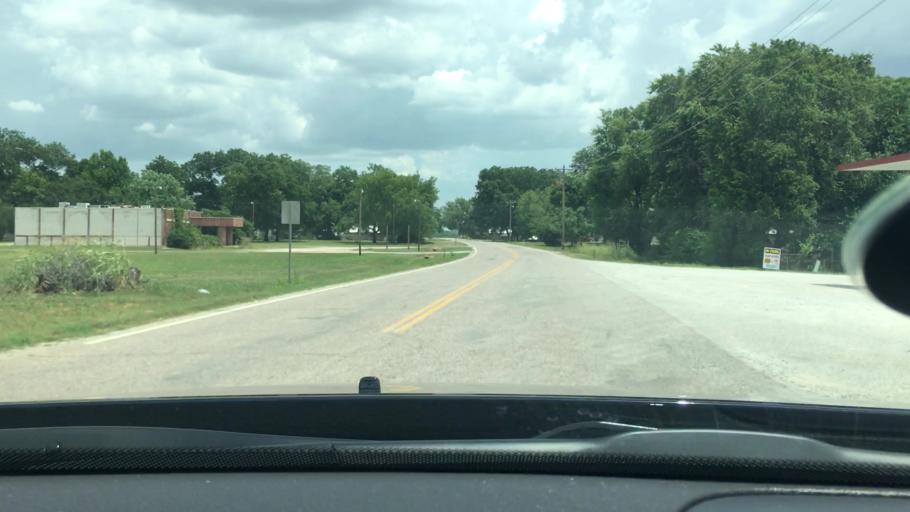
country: US
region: Texas
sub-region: Grayson County
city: Sherwood Shores
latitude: 33.9838
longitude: -96.9128
